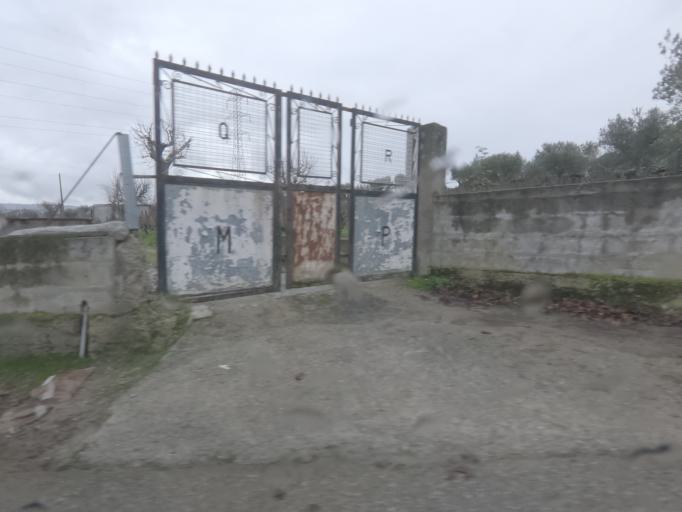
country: PT
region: Viseu
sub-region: Armamar
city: Armamar
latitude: 41.1625
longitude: -7.7118
